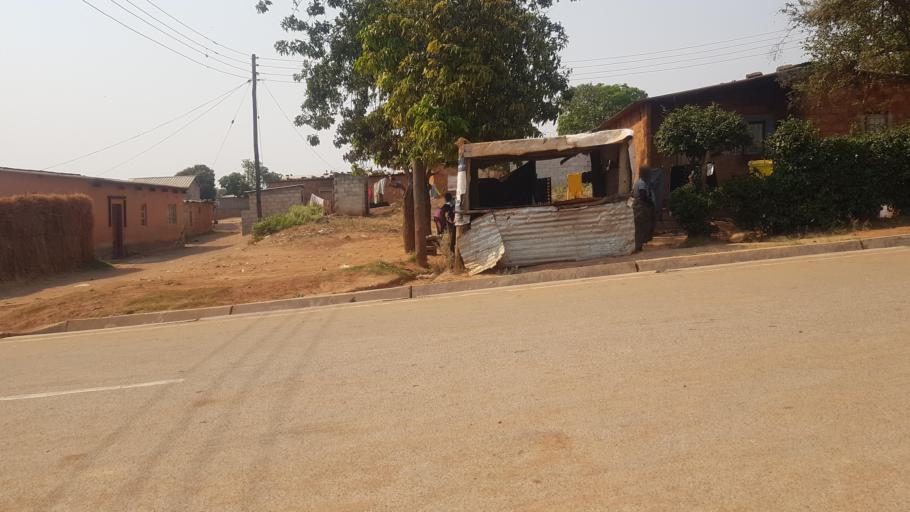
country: ZM
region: Lusaka
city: Lusaka
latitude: -15.4461
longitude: 28.3873
